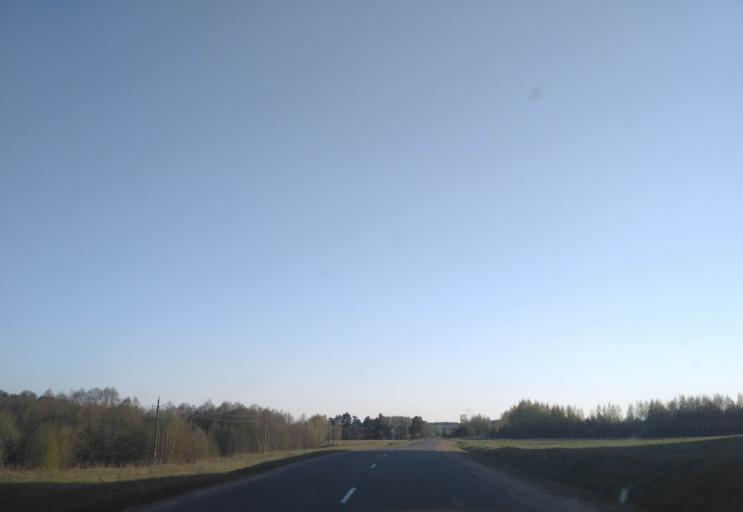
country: BY
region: Minsk
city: Radashkovichy
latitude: 54.1474
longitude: 27.2152
